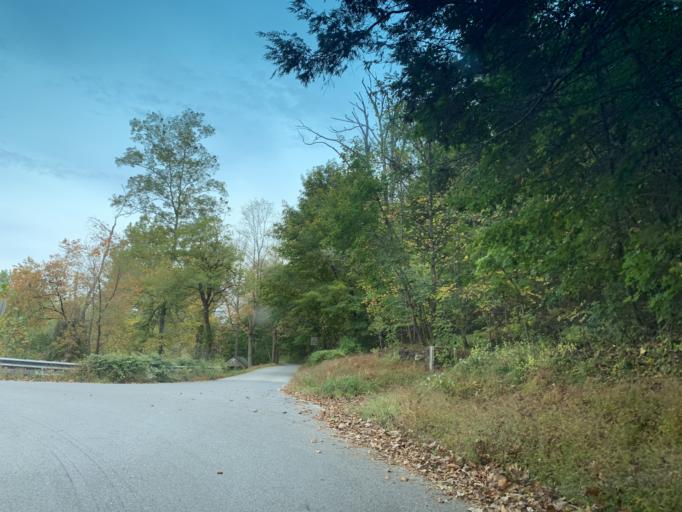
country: US
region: Pennsylvania
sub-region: York County
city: Stewartstown
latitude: 39.8254
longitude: -76.5105
